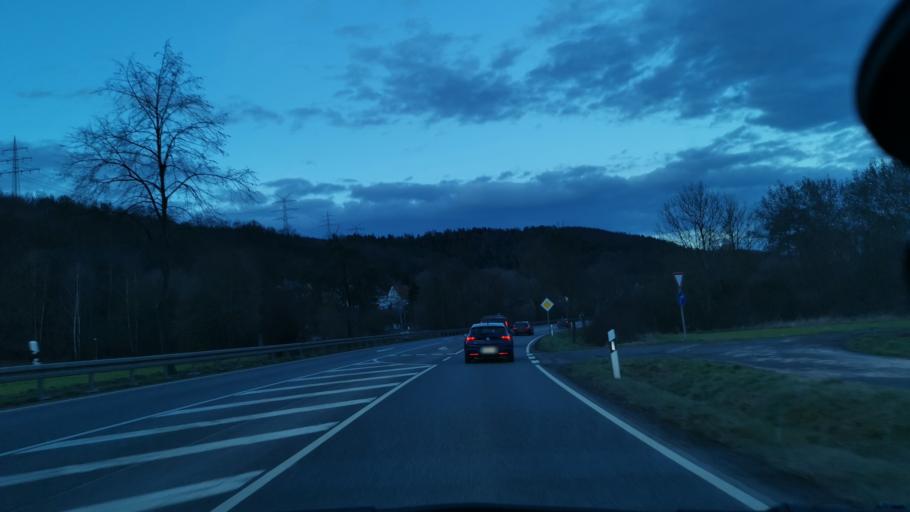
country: DE
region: Hesse
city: Breitenbach
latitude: 50.9196
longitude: 9.7496
